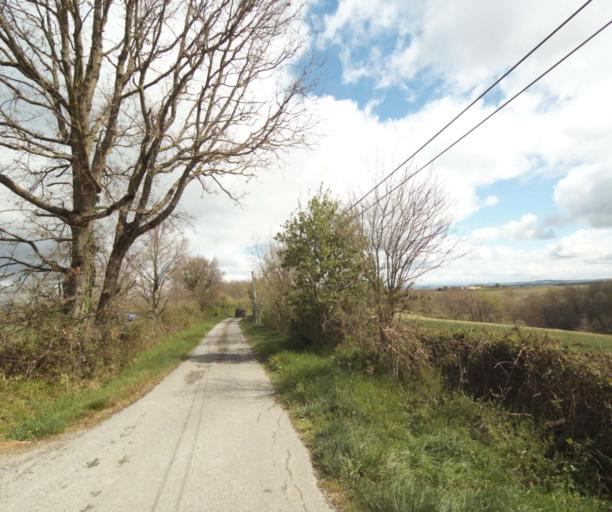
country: FR
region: Midi-Pyrenees
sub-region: Departement de l'Ariege
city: Saverdun
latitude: 43.1980
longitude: 1.5762
